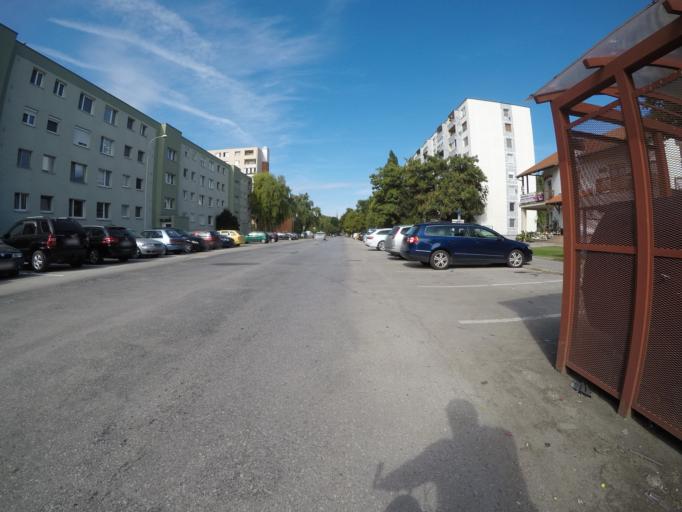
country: SK
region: Trnavsky
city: Dunajska Streda
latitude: 47.9918
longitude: 17.6262
